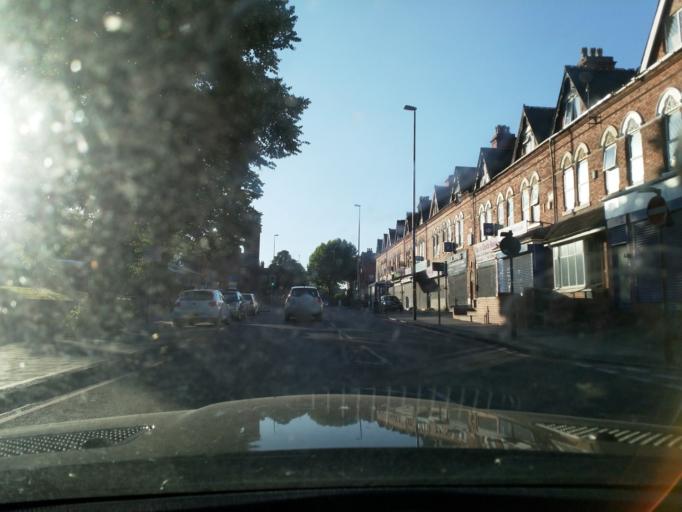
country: GB
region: England
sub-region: City and Borough of Birmingham
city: Acocks Green
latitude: 52.4486
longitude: -1.8623
